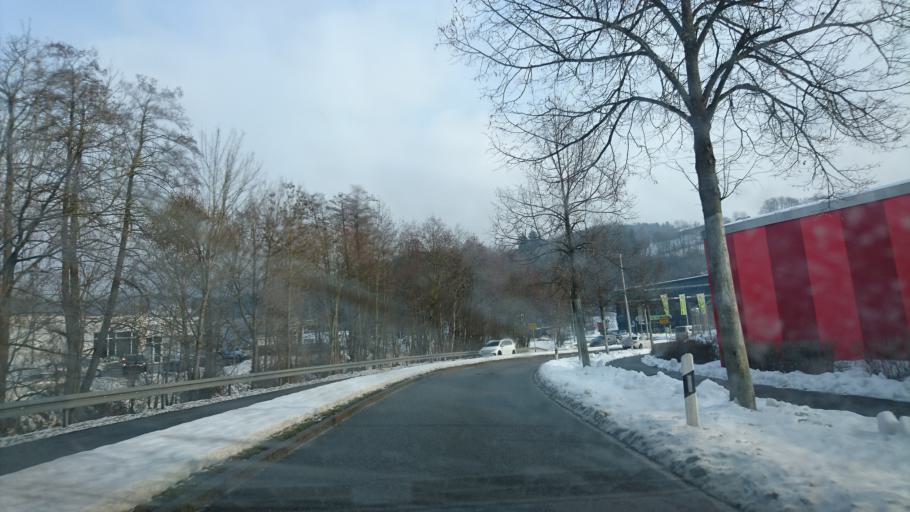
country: DE
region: Bavaria
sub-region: Lower Bavaria
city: Deggendorf
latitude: 48.8536
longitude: 12.9607
